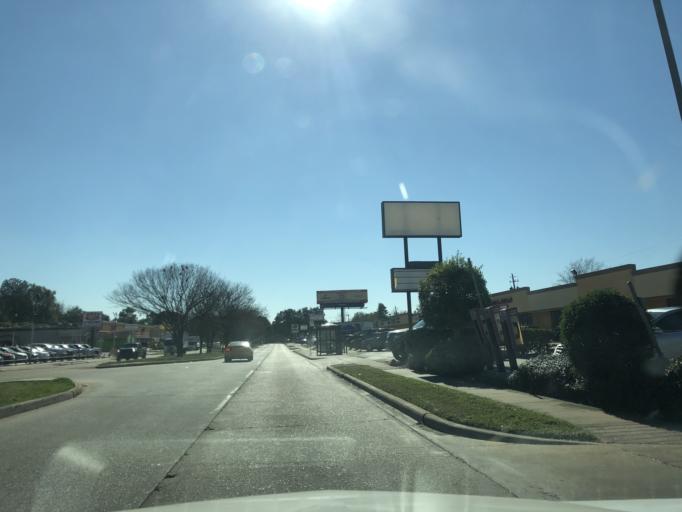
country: US
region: Texas
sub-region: Harris County
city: Bellaire
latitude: 29.6943
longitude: -95.4931
